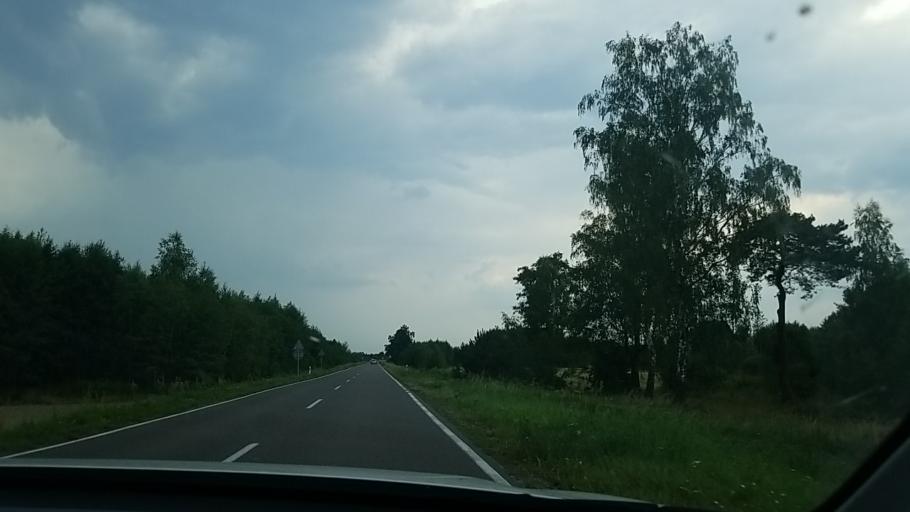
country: PL
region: Lublin Voivodeship
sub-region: Powiat swidnicki
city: Trawniki
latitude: 51.1884
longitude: 23.0547
